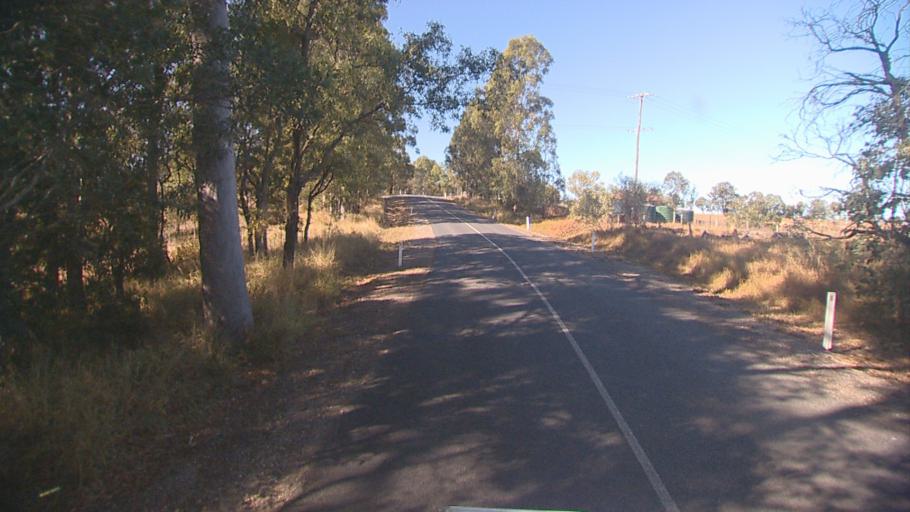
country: AU
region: Queensland
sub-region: Logan
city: Cedar Vale
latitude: -27.8980
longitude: 153.0157
